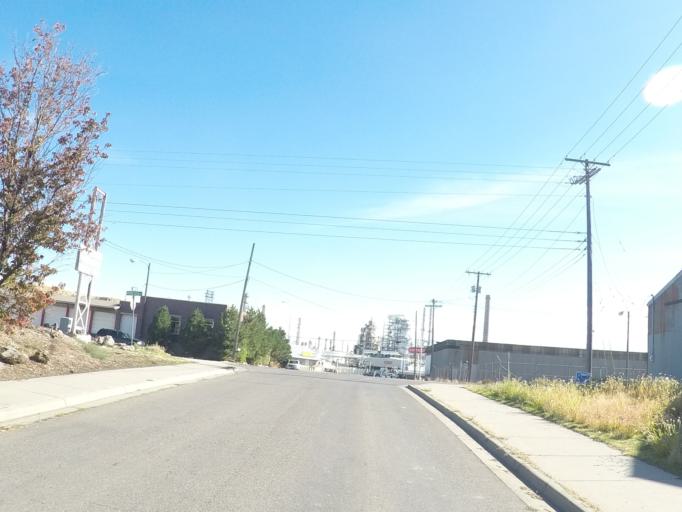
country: US
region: Montana
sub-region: Yellowstone County
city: Billings
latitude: 45.7849
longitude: -108.4958
